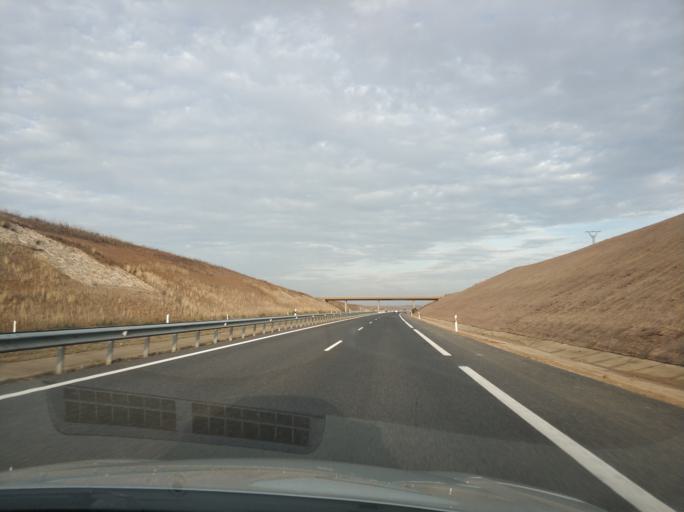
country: ES
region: Castille and Leon
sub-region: Provincia de Palencia
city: San Mames de Campos
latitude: 42.3659
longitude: -4.5495
